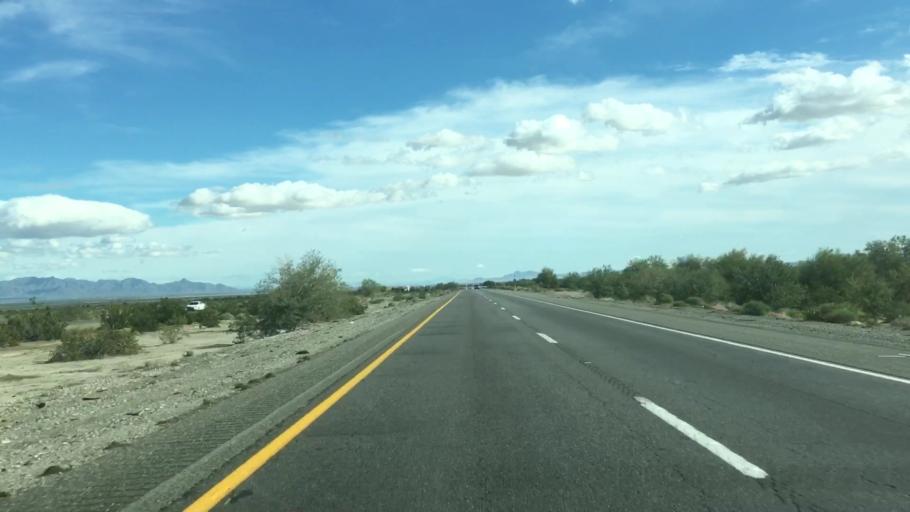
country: US
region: California
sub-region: Riverside County
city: Mesa Verde
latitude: 33.6608
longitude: -115.1707
